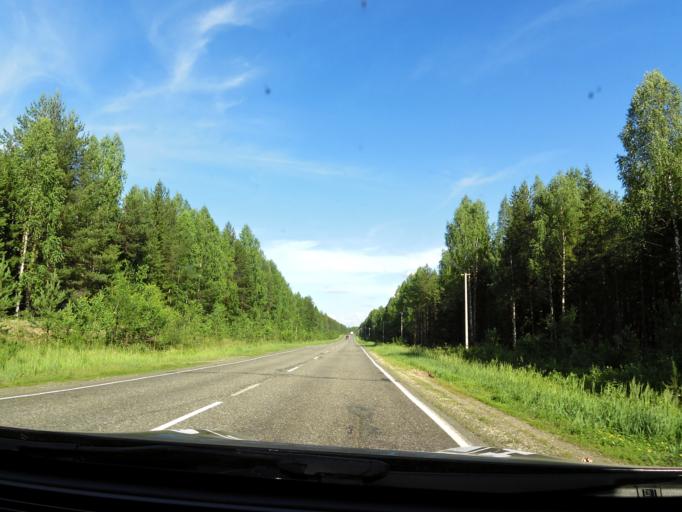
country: RU
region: Kirov
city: Belaya Kholunitsa
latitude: 58.9161
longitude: 51.1474
